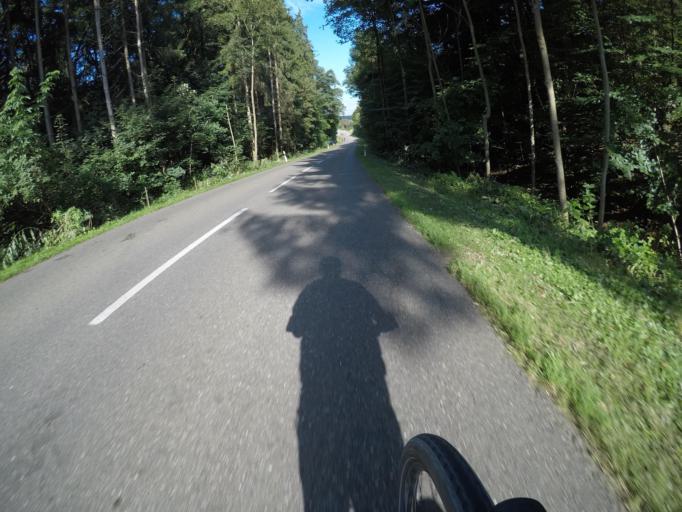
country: DE
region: Bavaria
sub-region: Swabia
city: Allmannshofen
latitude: 48.6164
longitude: 10.7783
